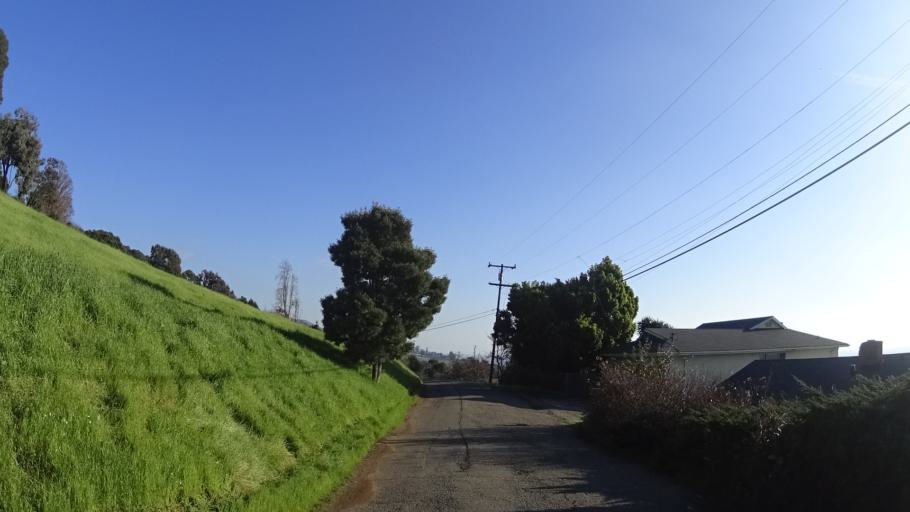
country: US
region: California
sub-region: Alameda County
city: Hayward
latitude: 37.6569
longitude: -122.0642
